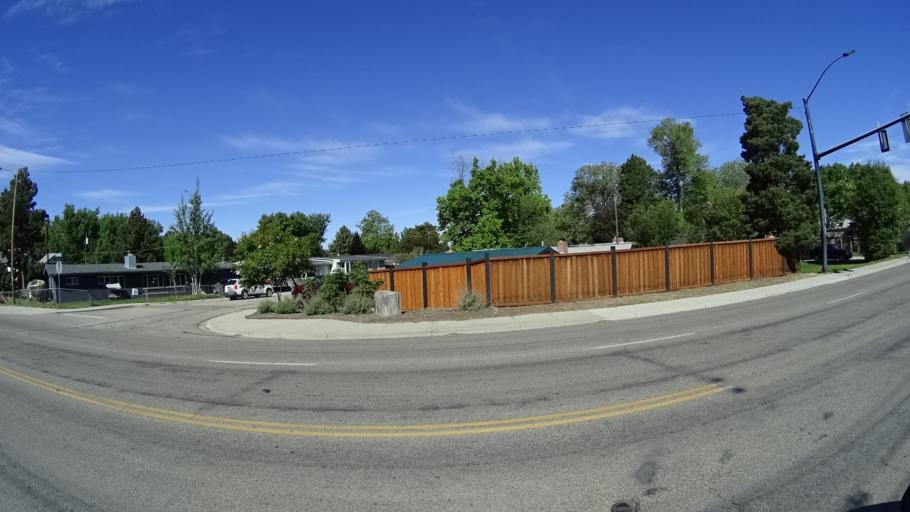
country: US
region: Idaho
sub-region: Ada County
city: Garden City
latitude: 43.5852
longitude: -116.2436
